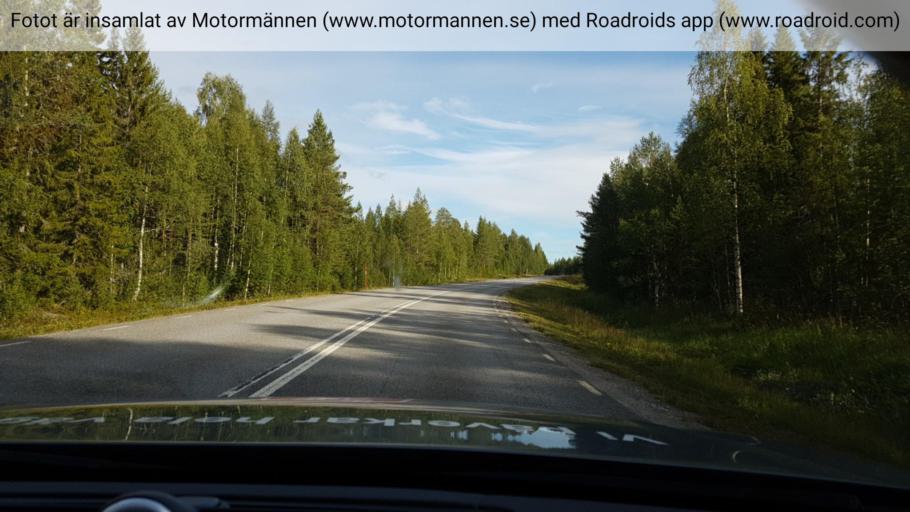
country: SE
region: Jaemtland
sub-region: Stroemsunds Kommun
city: Stroemsund
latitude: 64.3265
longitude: 15.1869
